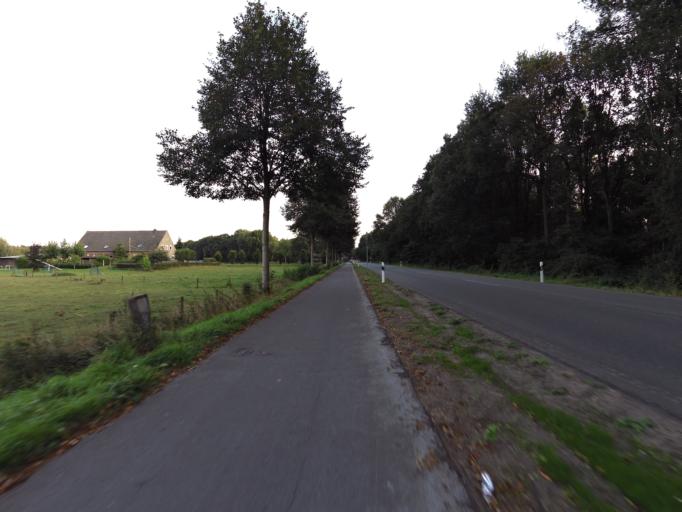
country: NL
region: Gelderland
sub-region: Gemeente Zevenaar
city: Zevenaar
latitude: 51.8900
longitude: 6.1487
